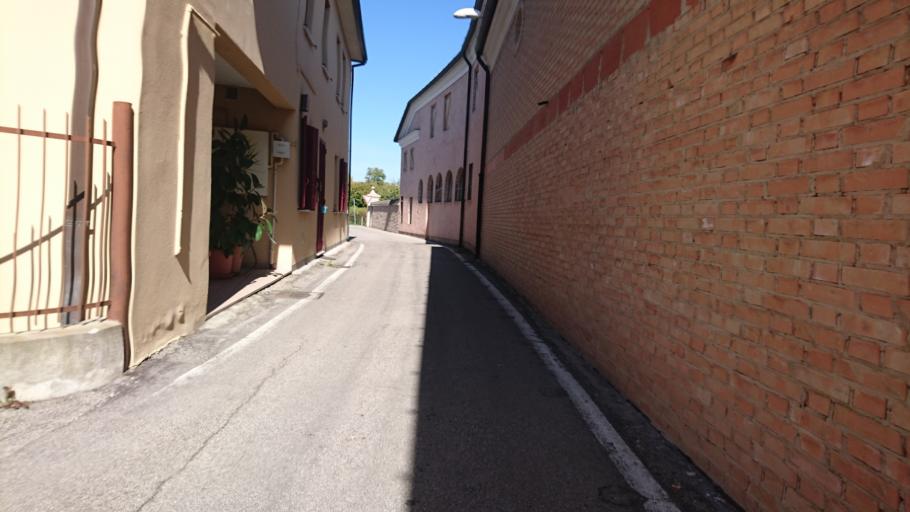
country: IT
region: Veneto
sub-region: Provincia di Venezia
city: Dolo
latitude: 45.4231
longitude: 12.0838
